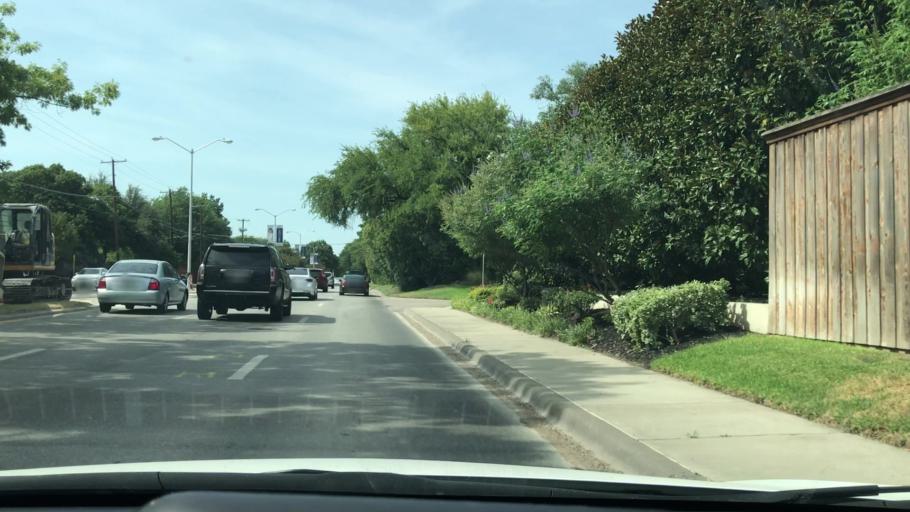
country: US
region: Texas
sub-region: Dallas County
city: University Park
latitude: 32.8870
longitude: -96.8039
